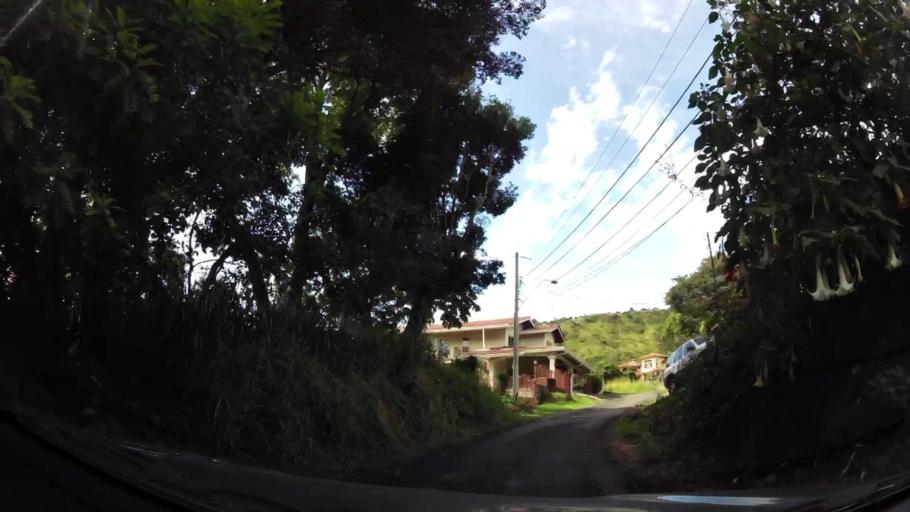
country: PA
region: Chiriqui
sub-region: Distrito Boquete
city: Boquete
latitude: 8.7686
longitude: -82.4350
